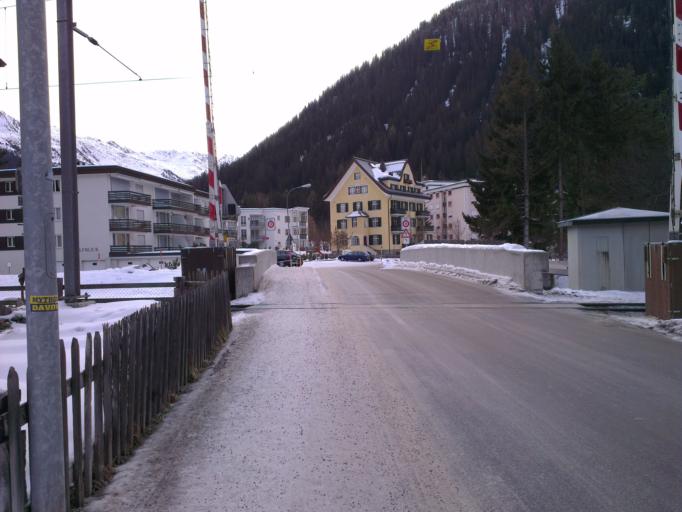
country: CH
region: Grisons
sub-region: Praettigau/Davos District
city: Davos
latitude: 46.7996
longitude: 9.8340
